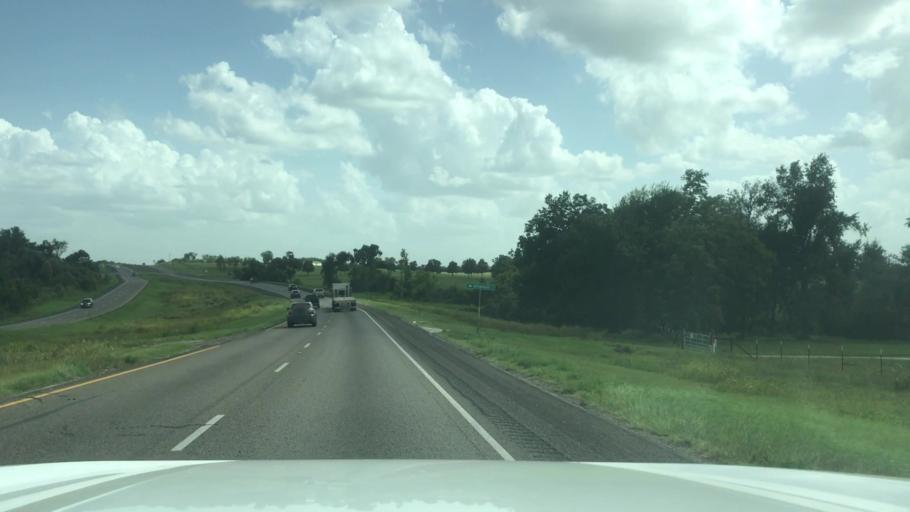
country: US
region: Texas
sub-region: Grimes County
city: Navasota
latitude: 30.3138
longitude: -96.0479
